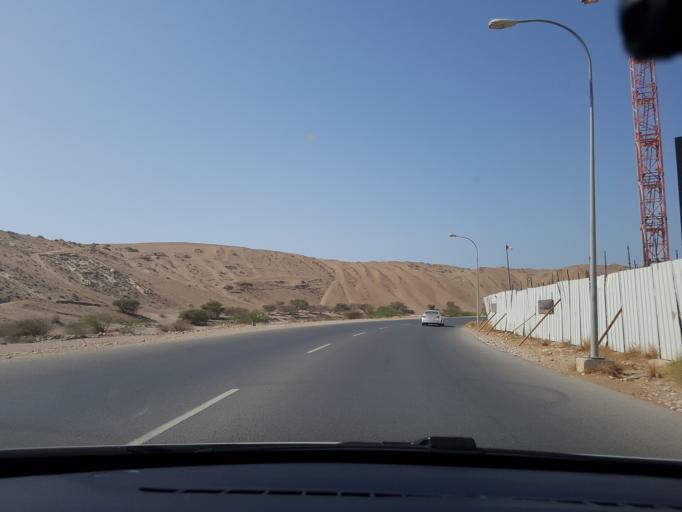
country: OM
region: Muhafazat Masqat
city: Bawshar
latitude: 23.5597
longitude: 58.4086
